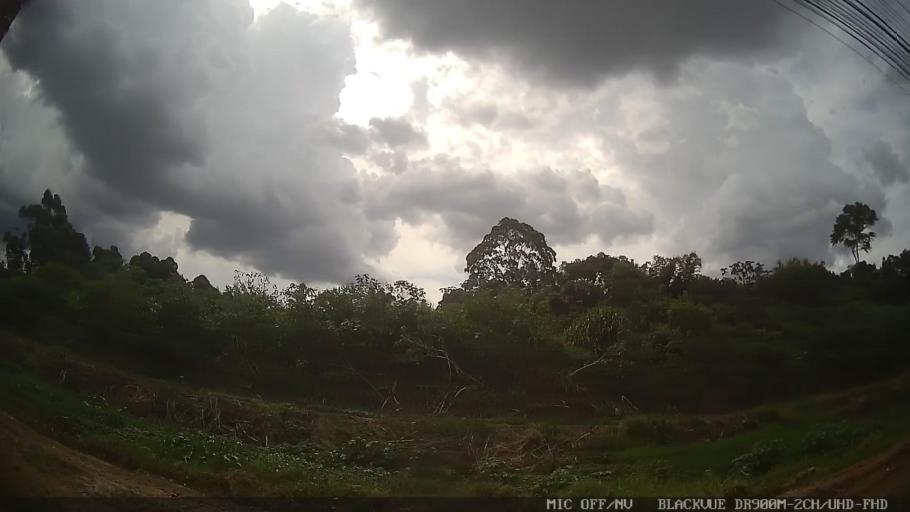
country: BR
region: Sao Paulo
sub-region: Poa
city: Poa
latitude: -23.5500
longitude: -46.3434
